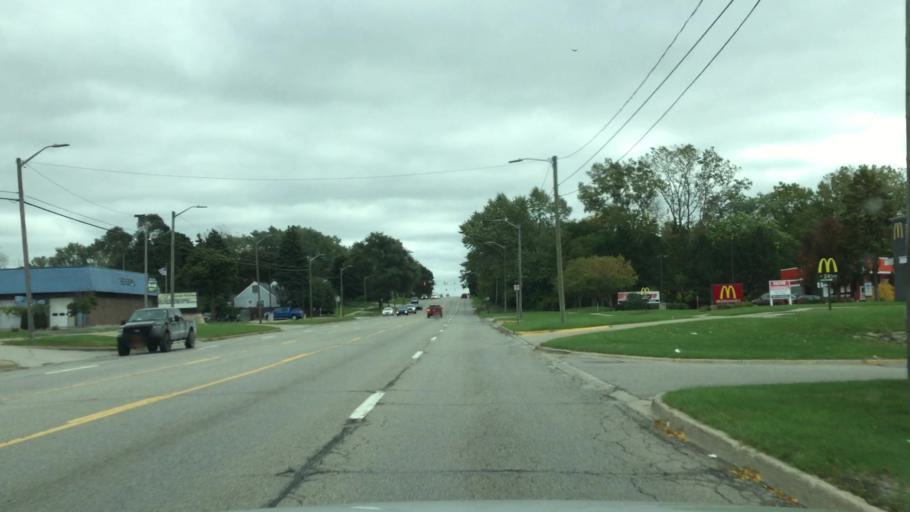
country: US
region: Michigan
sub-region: Oakland County
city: Keego Harbor
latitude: 42.6394
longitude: -83.3499
